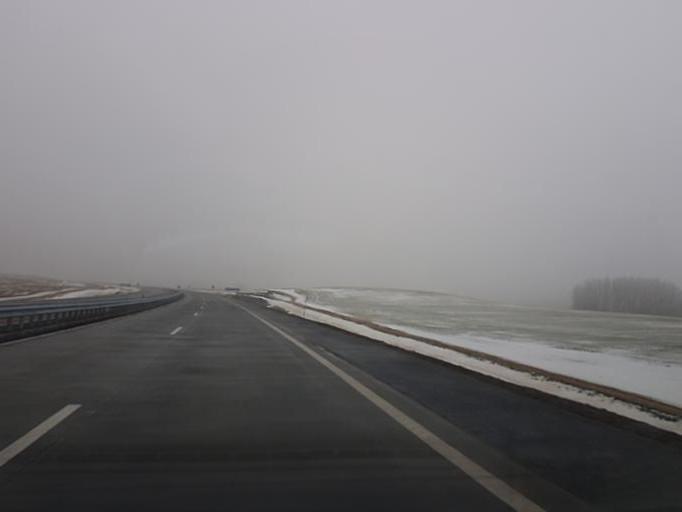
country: BY
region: Minsk
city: Atolina
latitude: 53.7557
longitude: 27.4089
